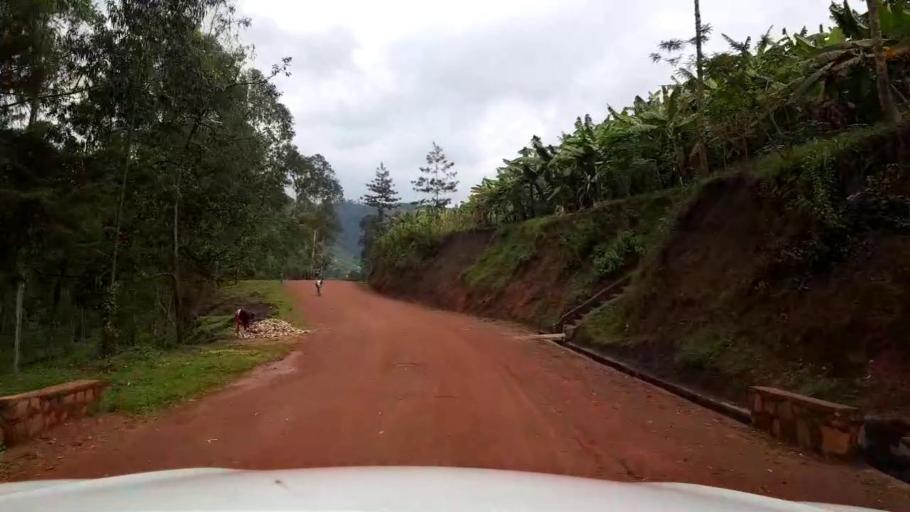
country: RW
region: Northern Province
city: Musanze
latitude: -1.6605
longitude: 29.8006
